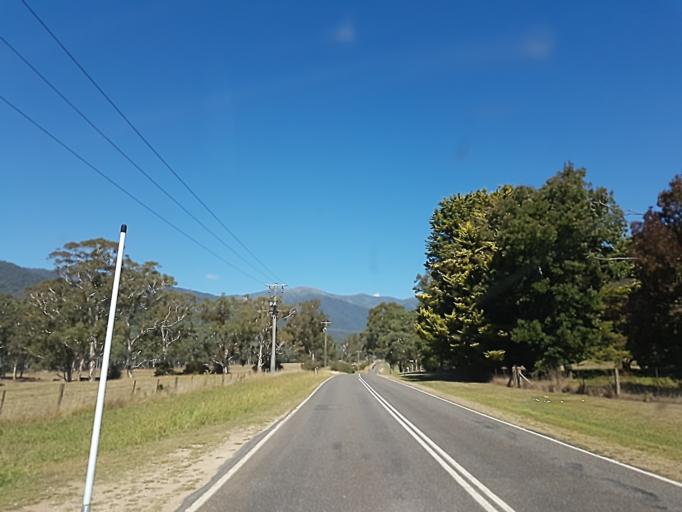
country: AU
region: Victoria
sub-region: Alpine
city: Mount Beauty
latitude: -36.8194
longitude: 147.0646
